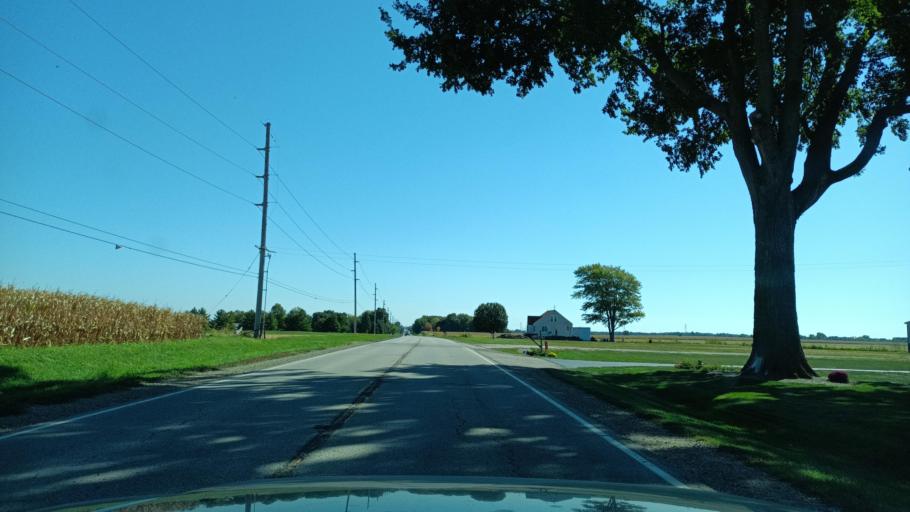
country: US
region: Illinois
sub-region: Peoria County
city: Dunlap
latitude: 40.7867
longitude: -89.7327
